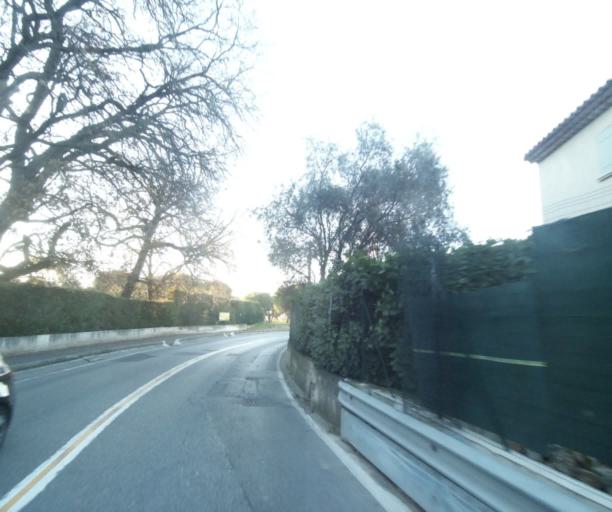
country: FR
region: Provence-Alpes-Cote d'Azur
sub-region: Departement des Alpes-Maritimes
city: Vallauris
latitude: 43.5771
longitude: 7.0879
